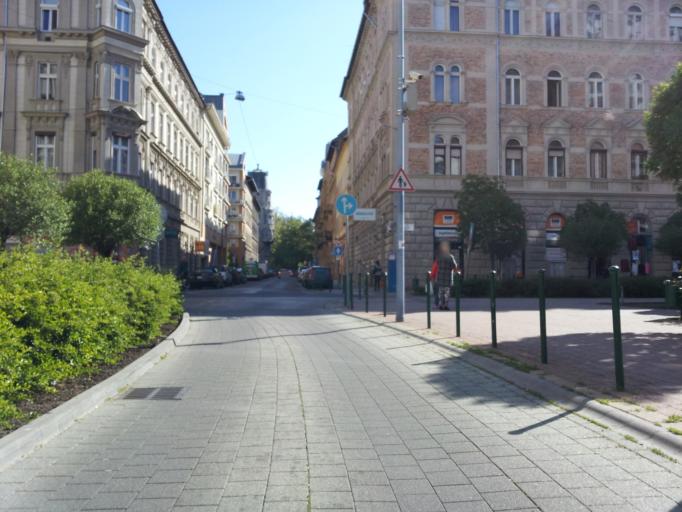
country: HU
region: Budapest
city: Budapest VII. keruelet
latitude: 47.5046
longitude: 19.0854
